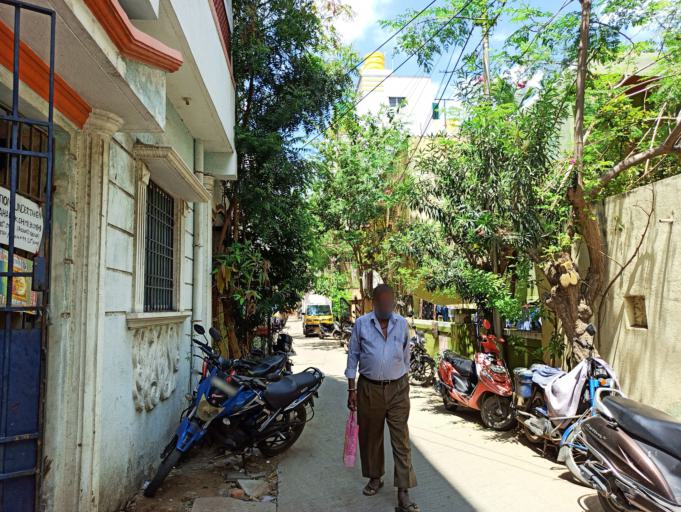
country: IN
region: Tamil Nadu
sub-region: Kancheepuram
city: Saint Thomas Mount
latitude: 13.0349
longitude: 80.1941
